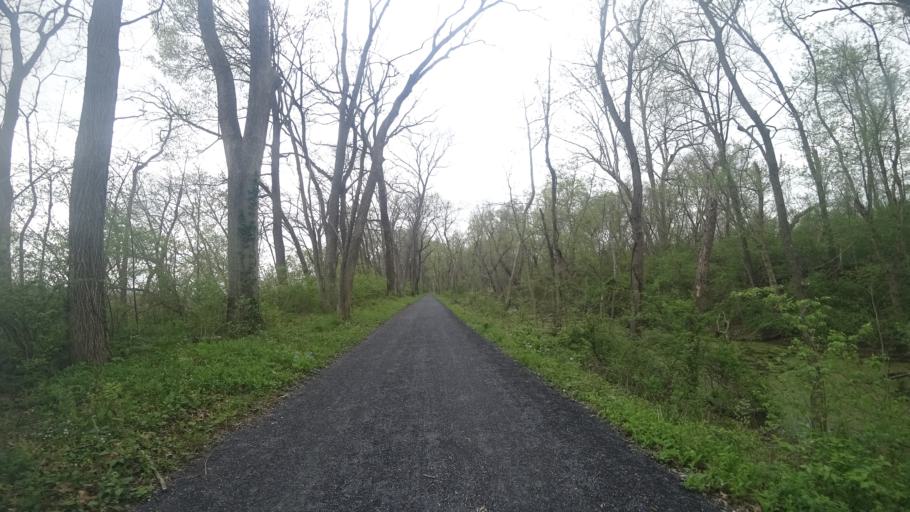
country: US
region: Virginia
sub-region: Loudoun County
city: University Center
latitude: 39.0748
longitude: -77.4221
